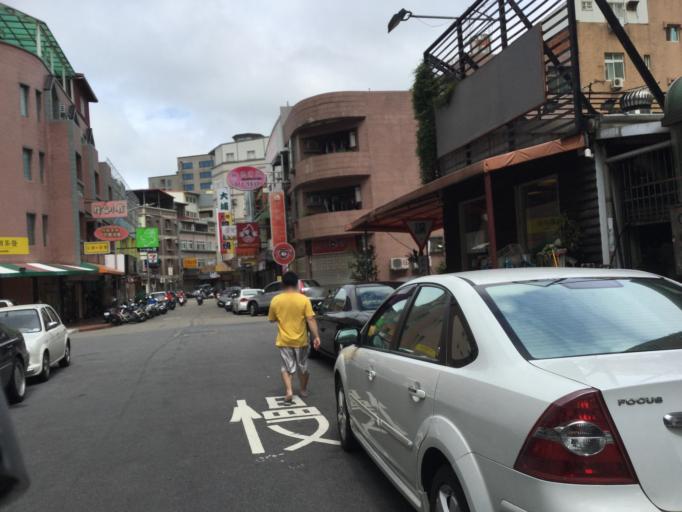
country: TW
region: Taiwan
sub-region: Hsinchu
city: Hsinchu
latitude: 24.7768
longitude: 121.0214
